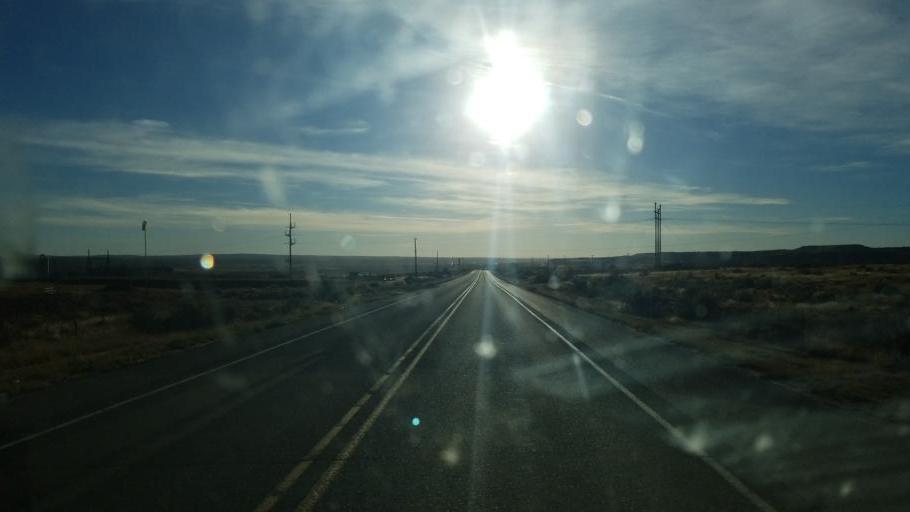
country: US
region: New Mexico
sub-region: San Juan County
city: Bloomfield
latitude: 36.7299
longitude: -107.7913
